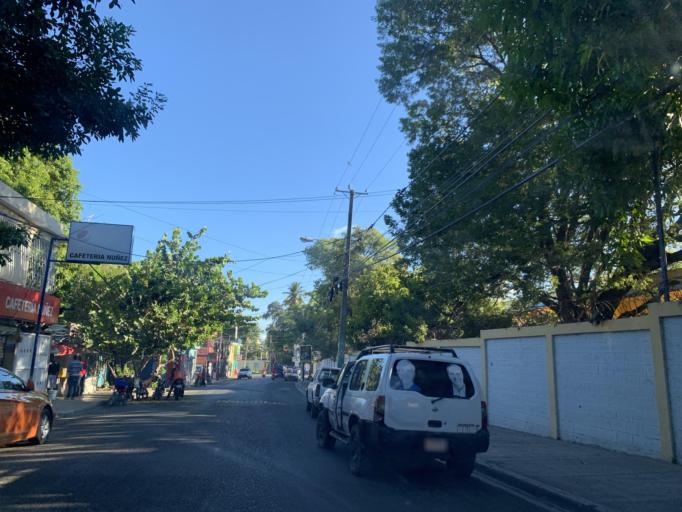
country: DO
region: Puerto Plata
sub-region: Puerto Plata
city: Puerto Plata
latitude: 19.7906
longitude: -70.6969
